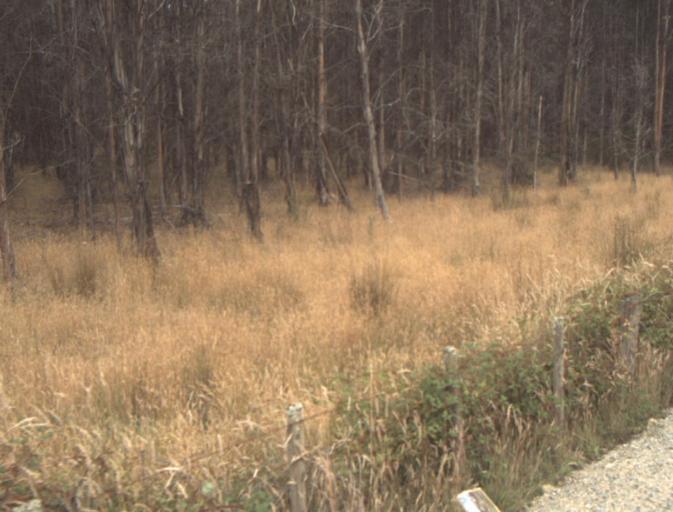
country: AU
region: Tasmania
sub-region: Launceston
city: Mayfield
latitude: -41.2144
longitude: 147.1912
